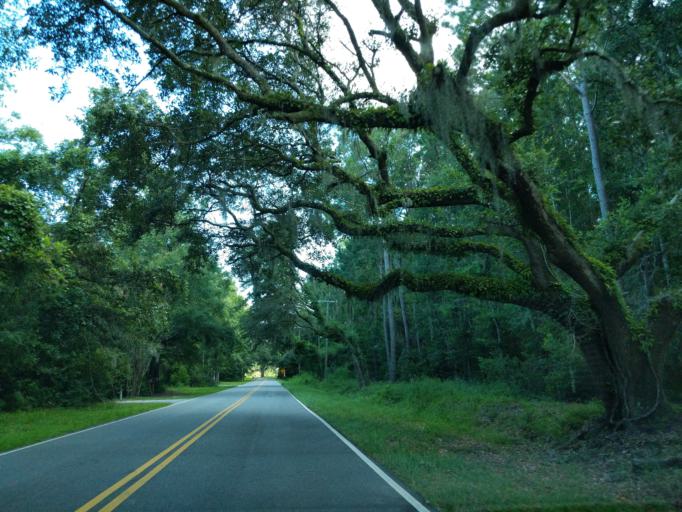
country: US
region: South Carolina
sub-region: Charleston County
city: Awendaw
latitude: 33.0952
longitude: -79.4657
